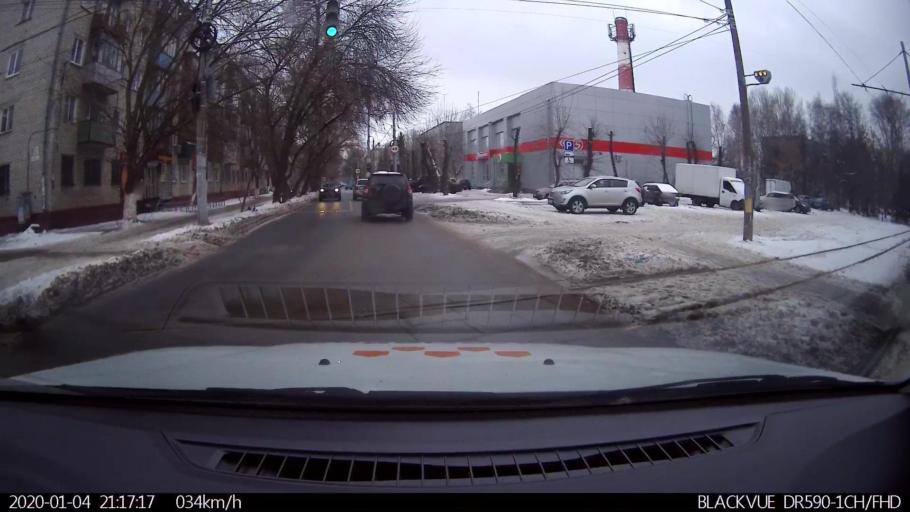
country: RU
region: Nizjnij Novgorod
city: Gorbatovka
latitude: 56.2348
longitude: 43.8522
